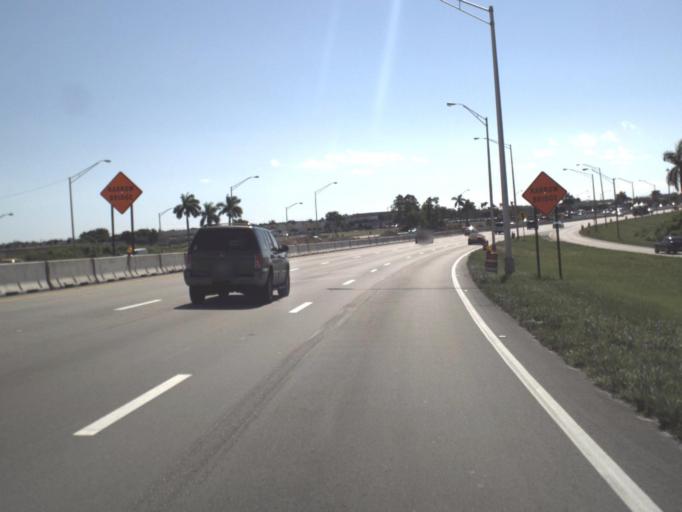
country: US
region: Florida
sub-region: Miami-Dade County
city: South Miami Heights
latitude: 25.5940
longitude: -80.3710
